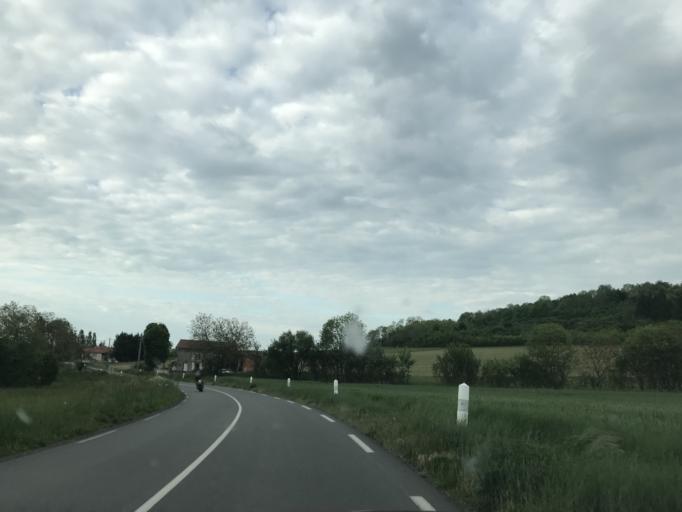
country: FR
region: Auvergne
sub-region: Departement du Puy-de-Dome
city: Maringues
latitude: 45.9619
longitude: 3.3375
